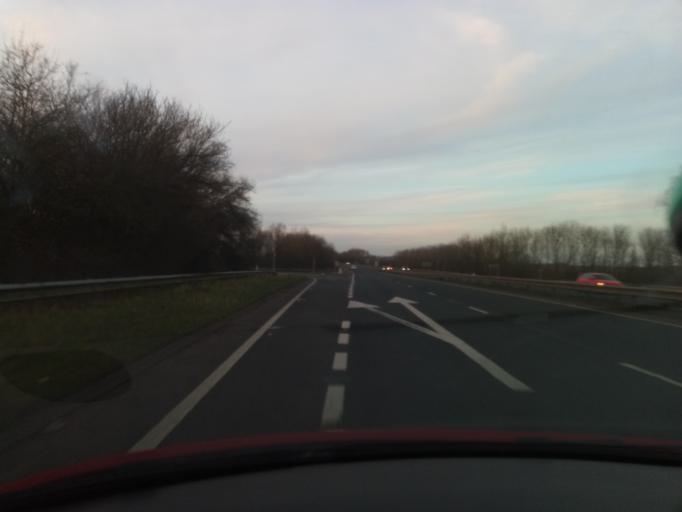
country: GB
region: England
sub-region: Leicestershire
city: Barrow upon Soar
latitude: 52.7337
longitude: -1.1357
